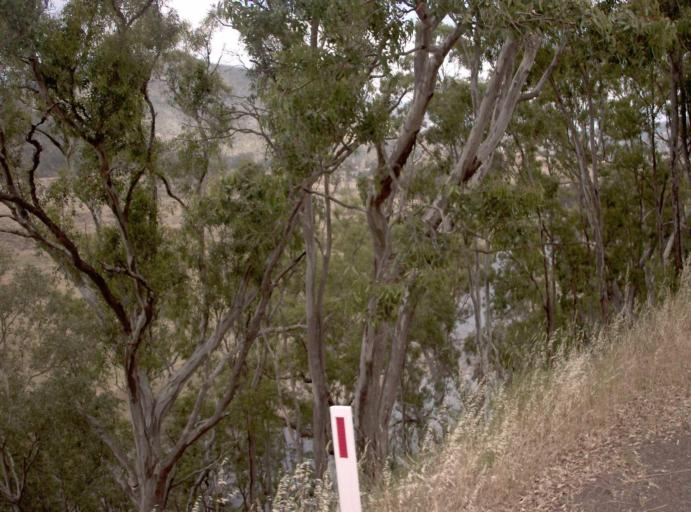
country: AU
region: Victoria
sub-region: Wellington
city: Heyfield
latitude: -37.6640
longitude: 146.6460
